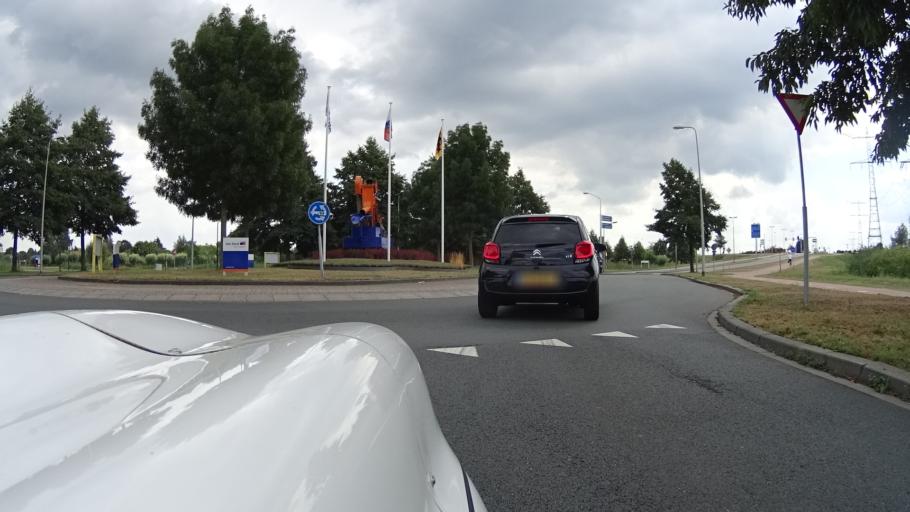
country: NL
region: South Holland
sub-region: Gemeente Sliedrecht
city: Sliedrecht
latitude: 51.8259
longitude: 4.8044
